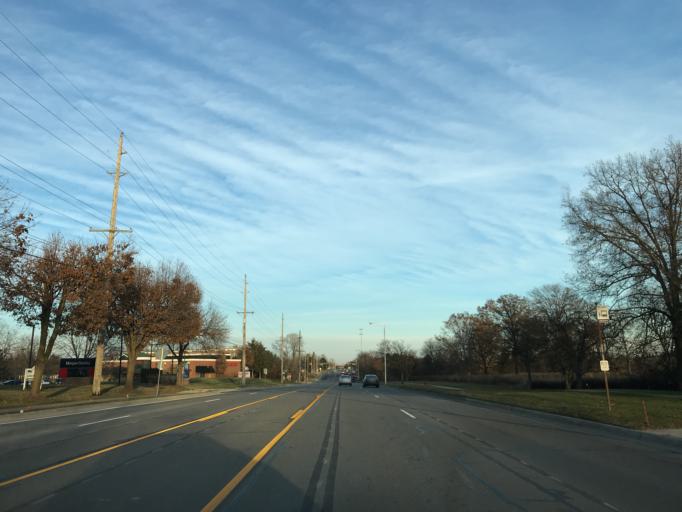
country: US
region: Michigan
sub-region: Washtenaw County
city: Ann Arbor
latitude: 42.3037
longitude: -83.6975
